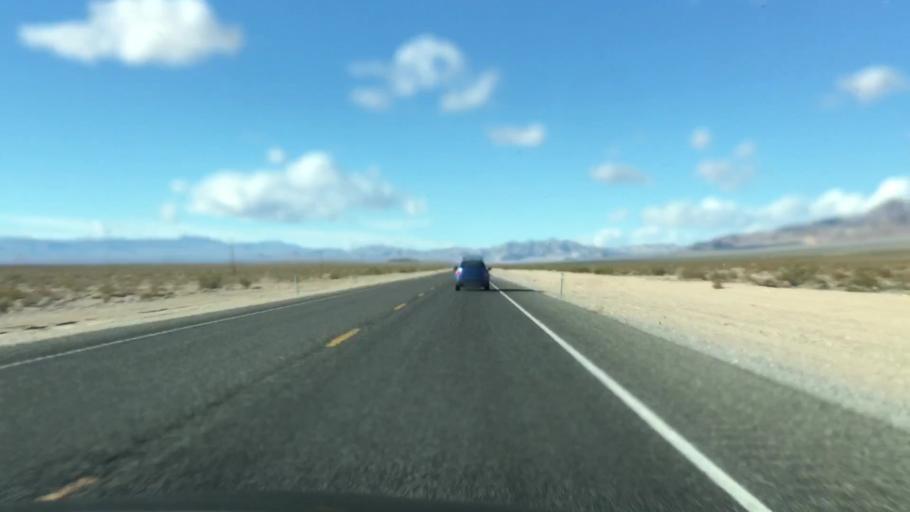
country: US
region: Nevada
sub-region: Nye County
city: Beatty
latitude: 36.7442
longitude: -116.6488
